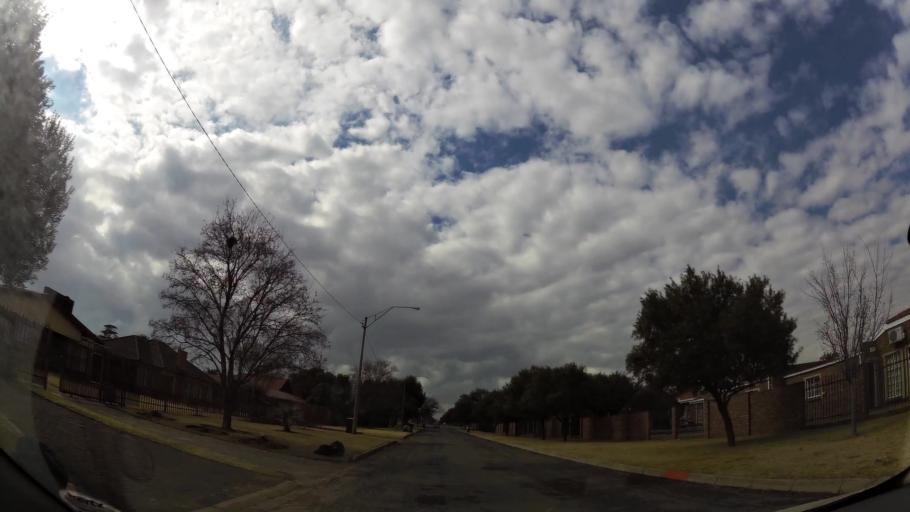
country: ZA
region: Gauteng
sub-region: Sedibeng District Municipality
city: Vereeniging
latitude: -26.6545
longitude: 27.9830
